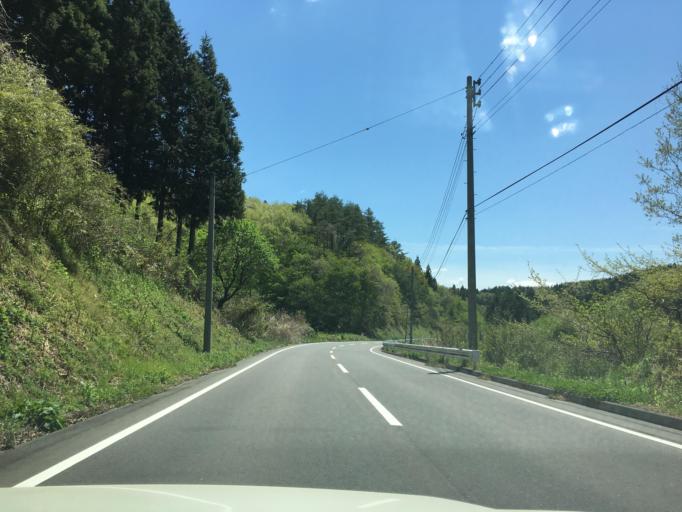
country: JP
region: Fukushima
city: Funehikimachi-funehiki
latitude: 37.3258
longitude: 140.6201
